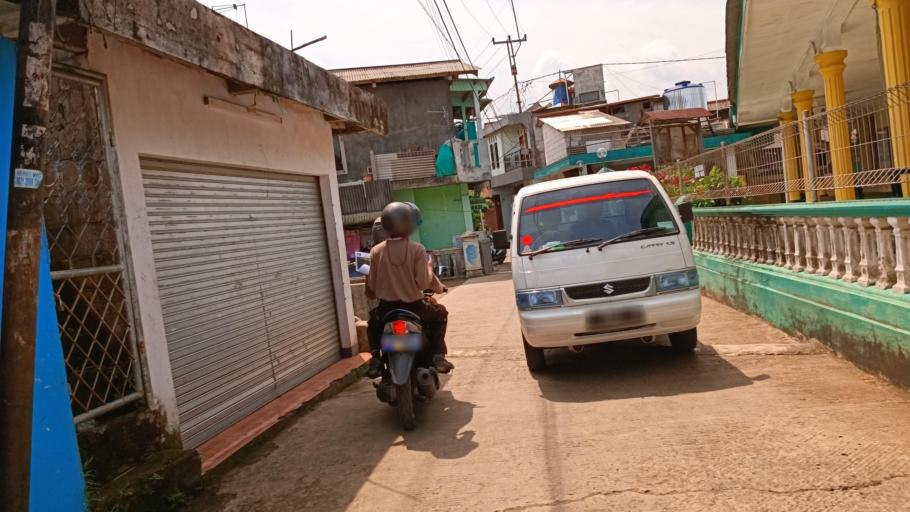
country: ID
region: West Java
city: Caringin
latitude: -6.6527
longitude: 106.8924
